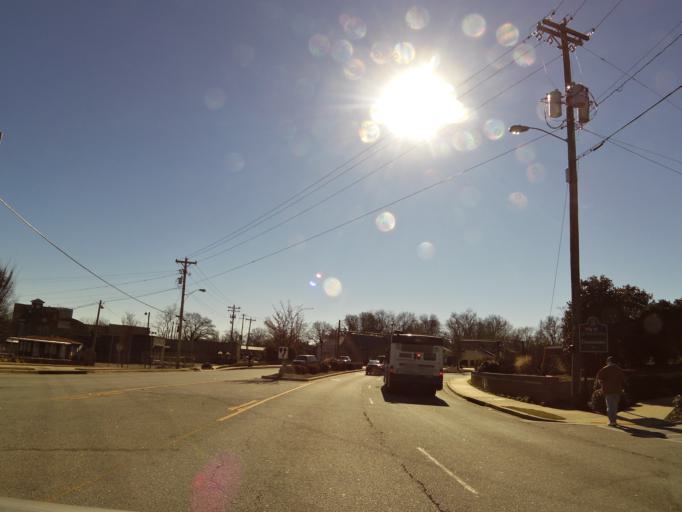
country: US
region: South Carolina
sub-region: Greenville County
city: Greenville
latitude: 34.8598
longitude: -82.4047
